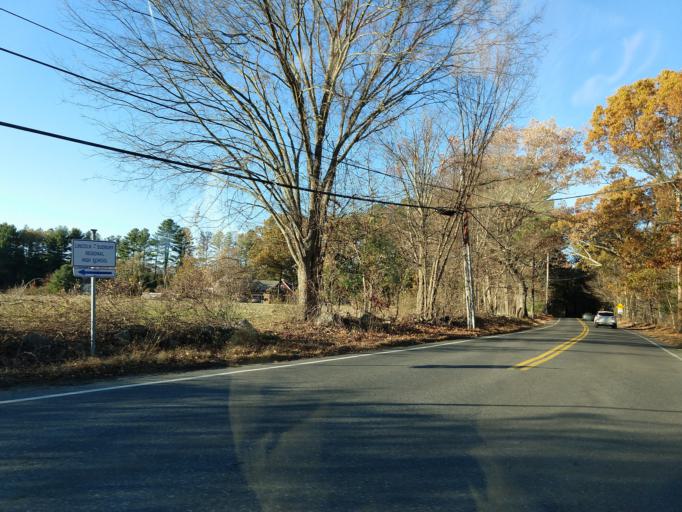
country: US
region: Massachusetts
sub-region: Middlesex County
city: Sudbury
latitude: 42.4069
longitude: -71.4035
